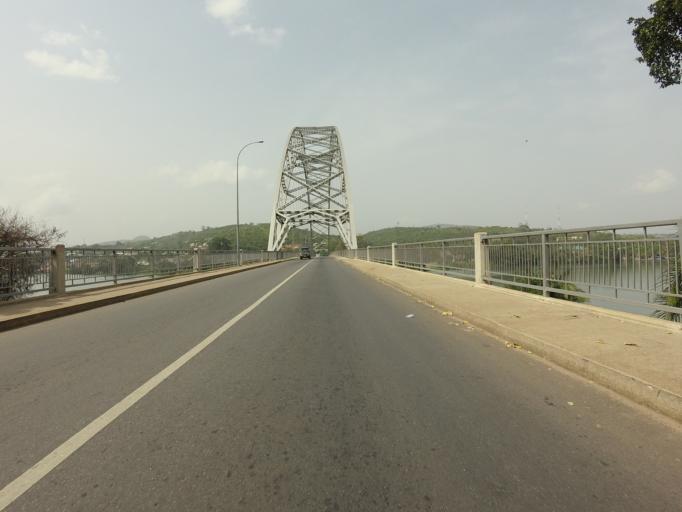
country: GH
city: Akropong
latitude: 6.2401
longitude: 0.0969
